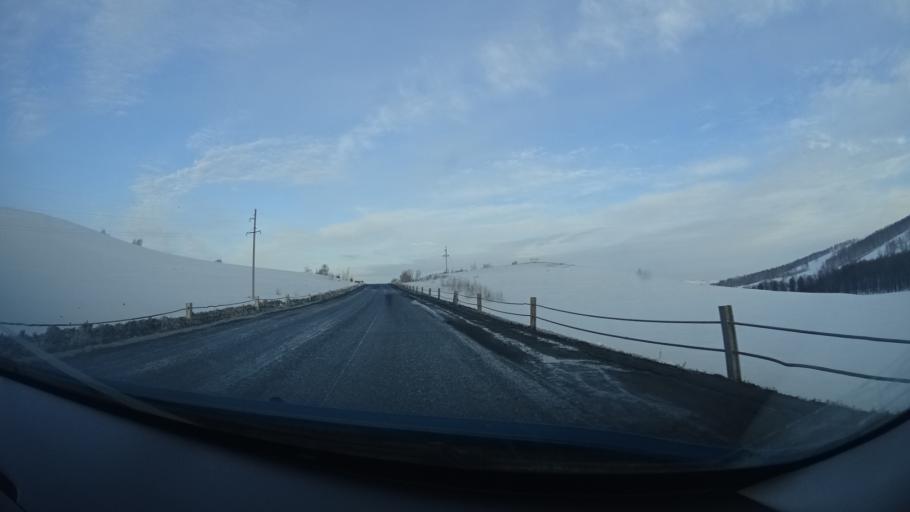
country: RU
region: Bashkortostan
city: Tubinskiy
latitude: 53.3164
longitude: 58.4918
